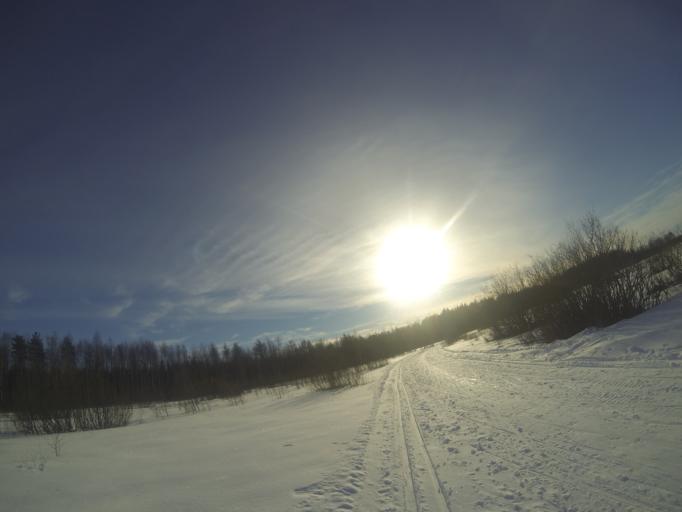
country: FI
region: Southern Savonia
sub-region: Savonlinna
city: Savonlinna
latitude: 61.9082
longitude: 28.9196
